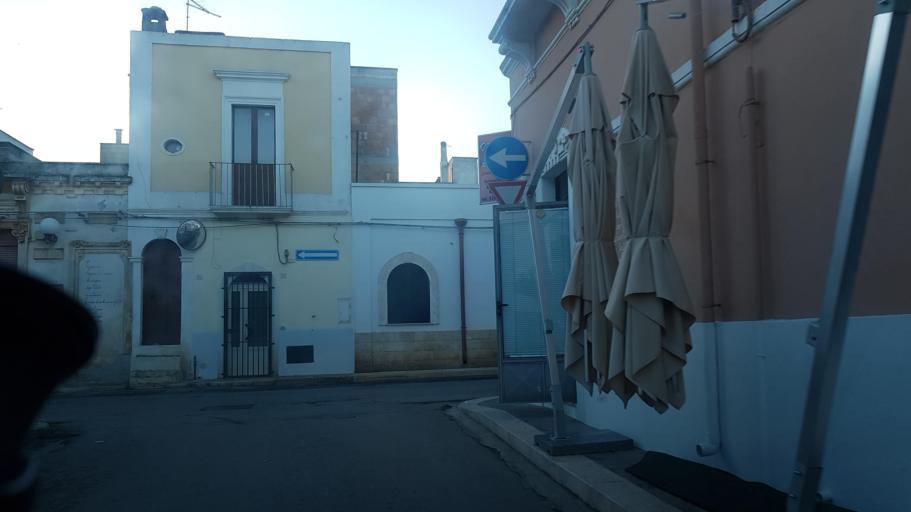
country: IT
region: Apulia
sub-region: Provincia di Brindisi
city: San Michele Salentino
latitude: 40.6319
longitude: 17.6324
